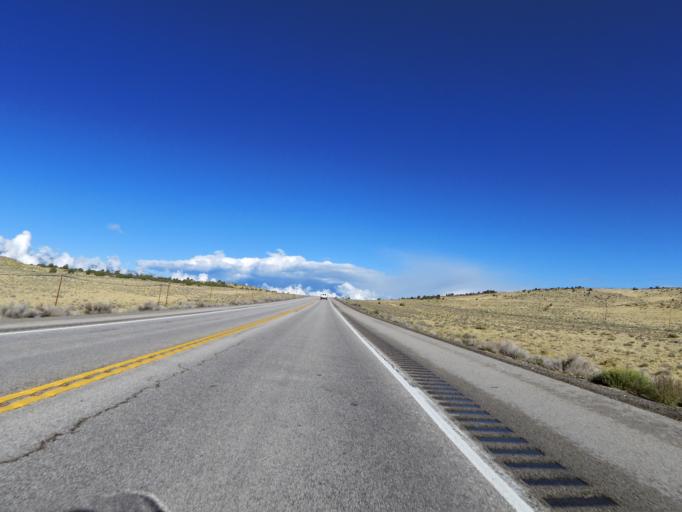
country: US
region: Nevada
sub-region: Douglas County
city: Gardnerville Ranchos
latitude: 38.8593
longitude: -119.6680
